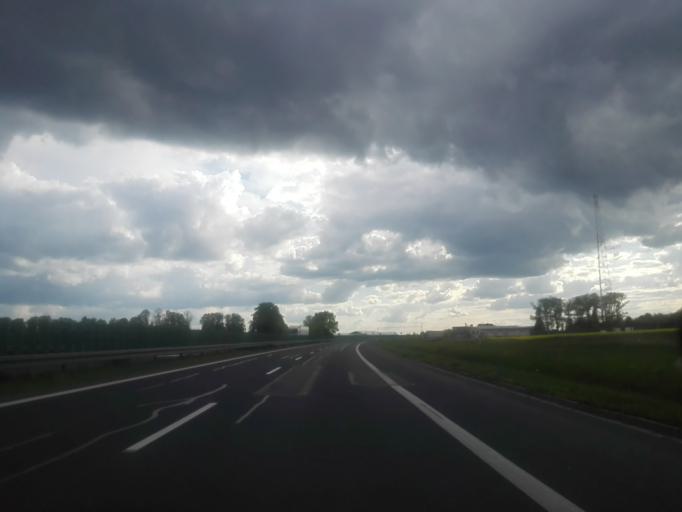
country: PL
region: Masovian Voivodeship
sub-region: Powiat ostrowski
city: Ostrow Mazowiecka
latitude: 52.8230
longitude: 21.9290
